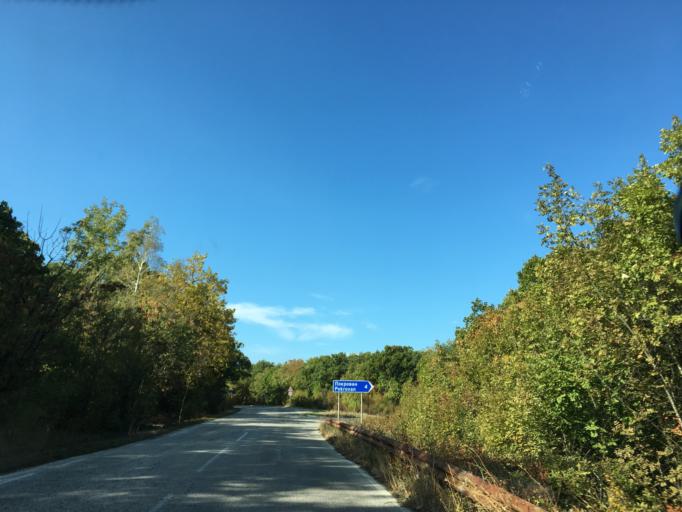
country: BG
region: Khaskovo
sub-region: Obshtina Ivaylovgrad
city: Ivaylovgrad
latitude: 41.5367
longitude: 26.0770
